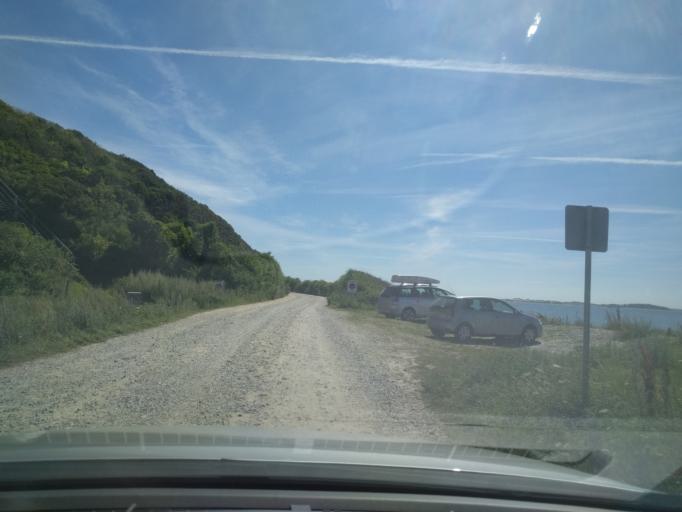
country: DK
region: South Denmark
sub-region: Kerteminde Kommune
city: Munkebo
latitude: 55.6094
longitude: 10.6006
